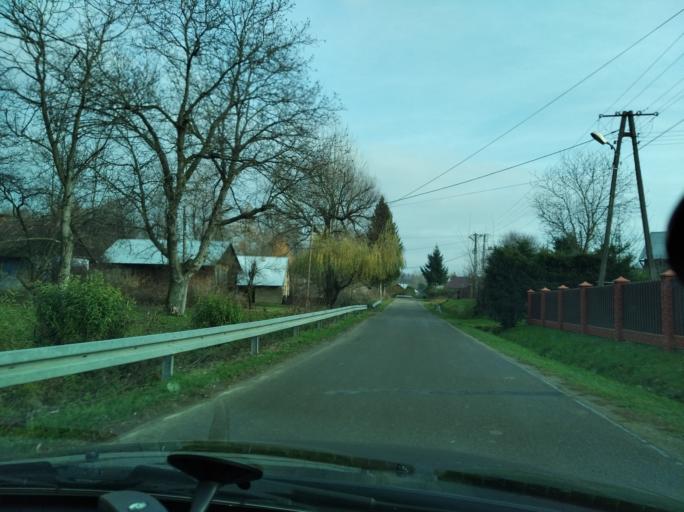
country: PL
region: Subcarpathian Voivodeship
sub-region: Powiat przeworski
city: Siedleczka
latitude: 49.9657
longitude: 22.3683
